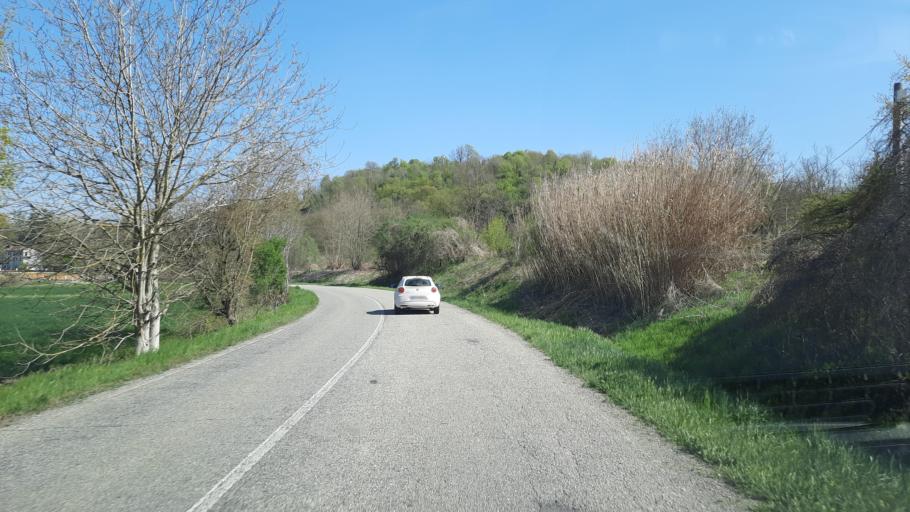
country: IT
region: Piedmont
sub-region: Provincia di Alessandria
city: Frassinello Monferrato
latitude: 45.0196
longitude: 8.3870
